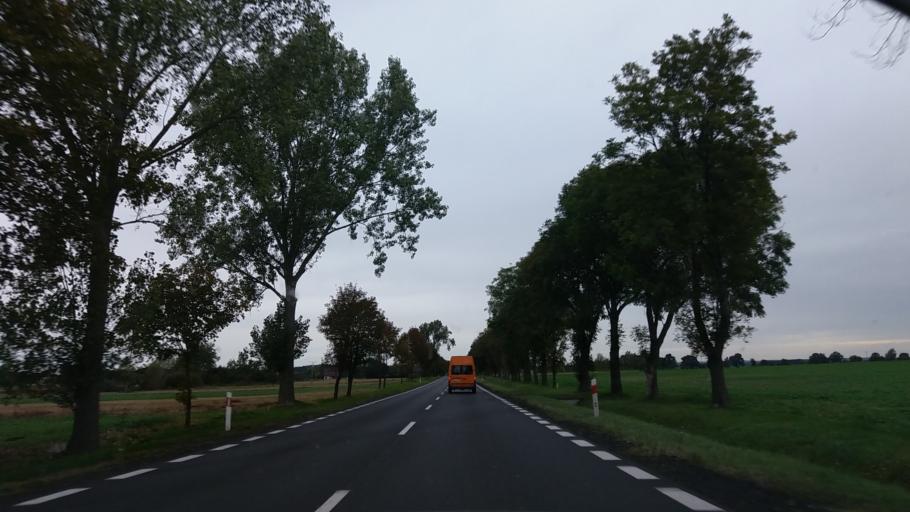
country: PL
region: Lower Silesian Voivodeship
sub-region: Powiat legnicki
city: Prochowice
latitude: 51.3273
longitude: 16.3104
